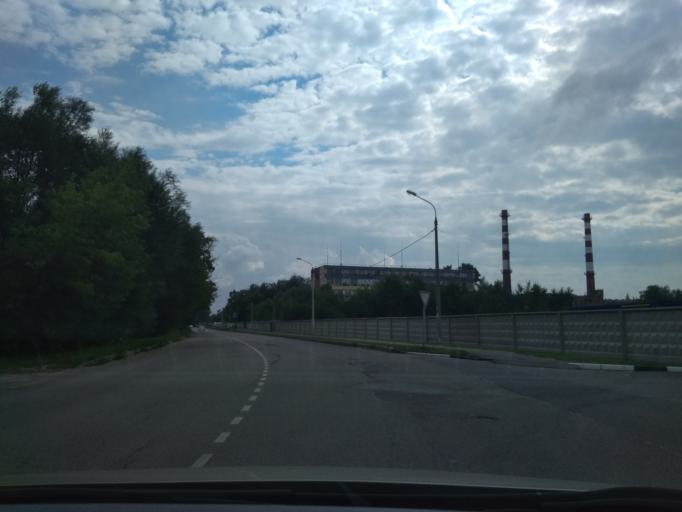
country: RU
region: Moskovskaya
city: Orekhovo-Zuyevo
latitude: 55.8008
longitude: 38.9490
